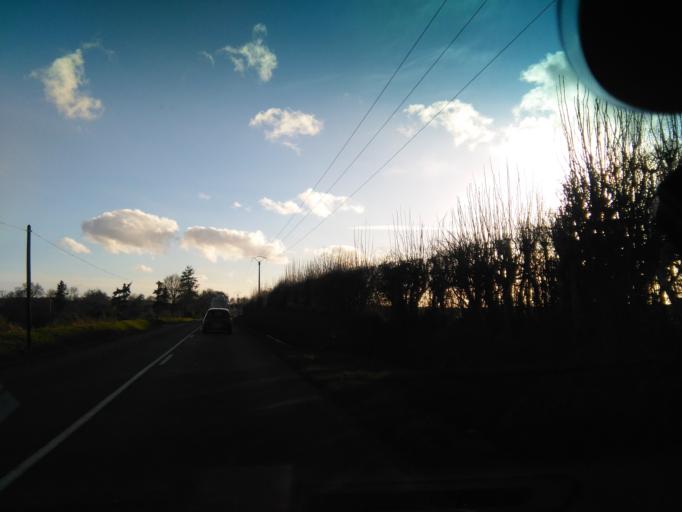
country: FR
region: Lower Normandy
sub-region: Departement de l'Orne
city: Pont-Ecrepin
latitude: 48.7139
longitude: -0.2735
